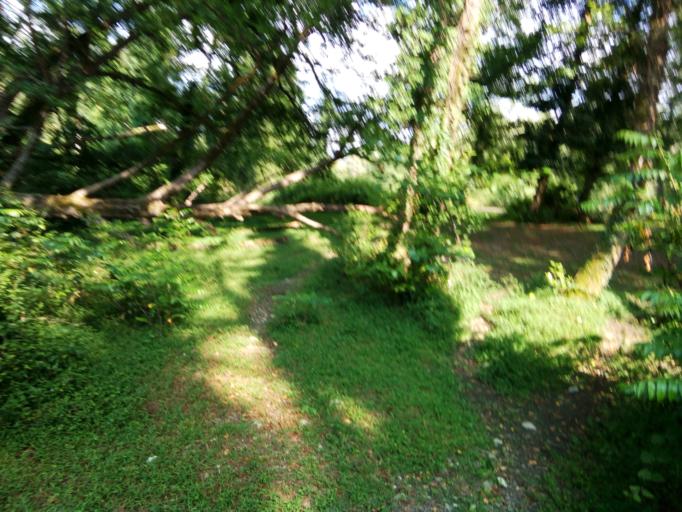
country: RU
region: Krasnodarskiy
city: Vardane
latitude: 43.8399
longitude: 39.5290
